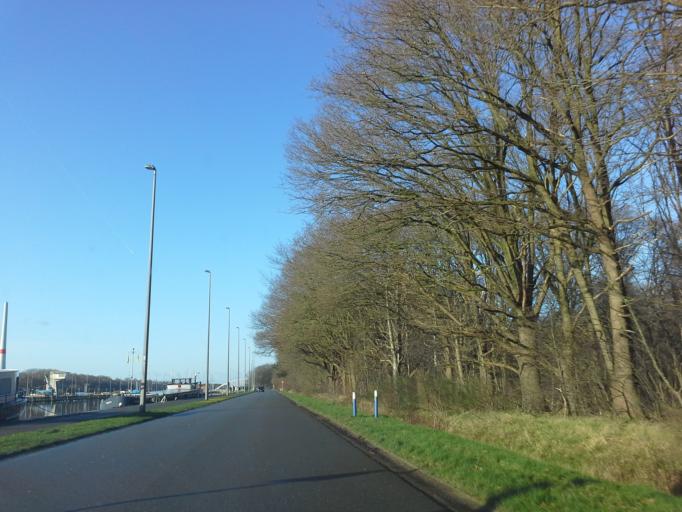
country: BE
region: Flanders
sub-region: Provincie Antwerpen
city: Olen
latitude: 51.1581
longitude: 4.8670
